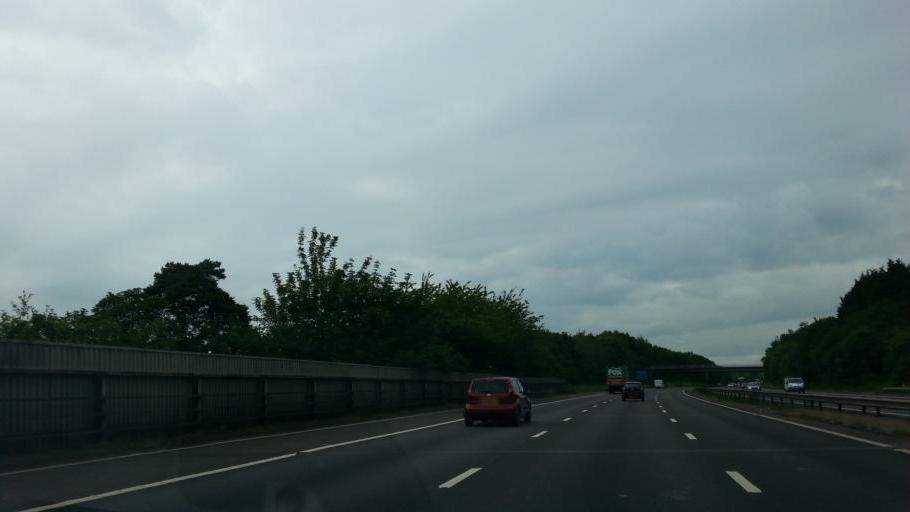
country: GB
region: England
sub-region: Worcestershire
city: Alvechurch
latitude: 52.3567
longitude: -1.9737
